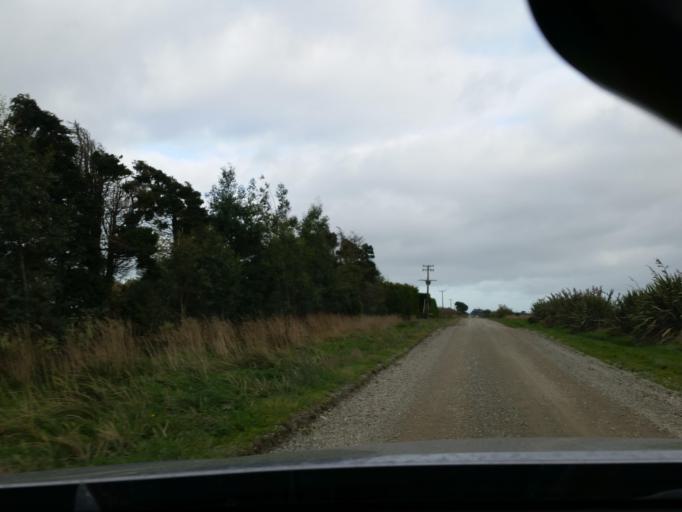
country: NZ
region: Southland
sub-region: Southland District
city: Winton
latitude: -46.2459
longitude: 168.3672
